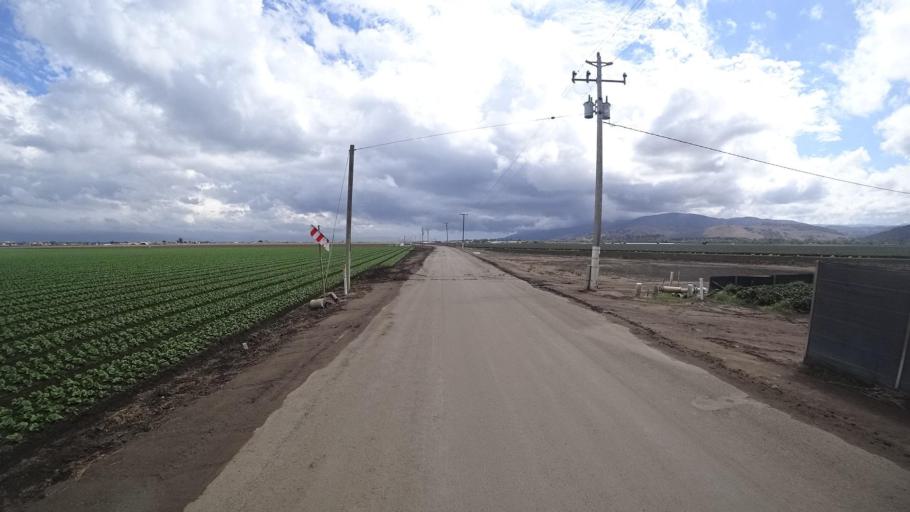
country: US
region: California
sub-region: Monterey County
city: Salinas
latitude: 36.6459
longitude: -121.6855
